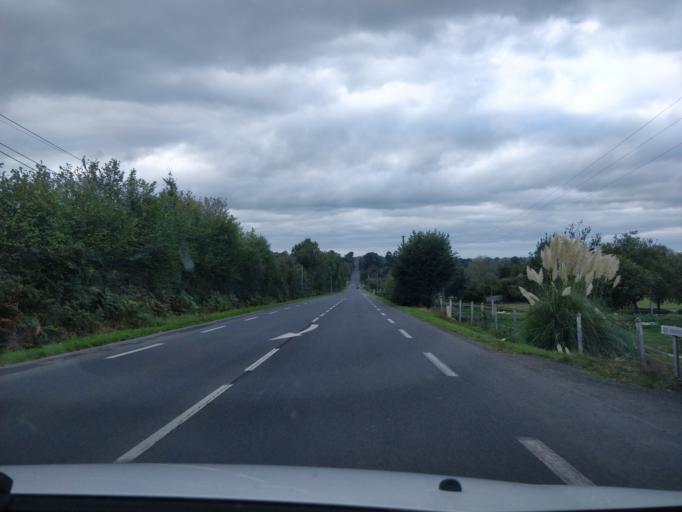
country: FR
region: Lower Normandy
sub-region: Departement de la Manche
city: Villedieu-les-Poeles
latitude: 48.8269
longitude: -1.1501
